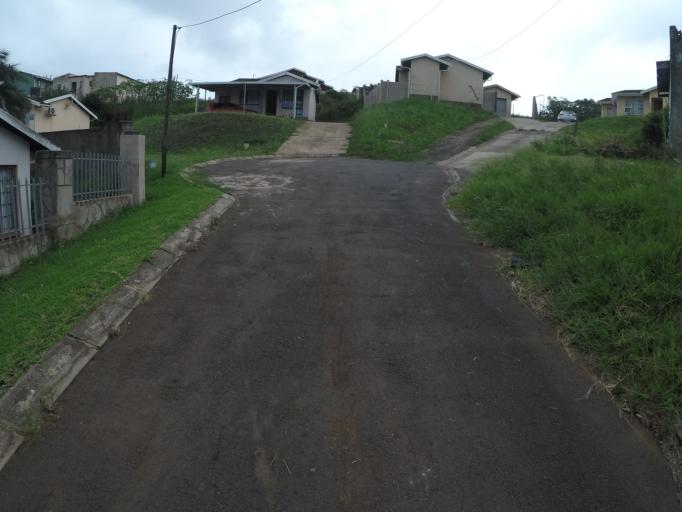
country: ZA
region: KwaZulu-Natal
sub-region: uThungulu District Municipality
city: Empangeni
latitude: -28.7692
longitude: 31.8611
